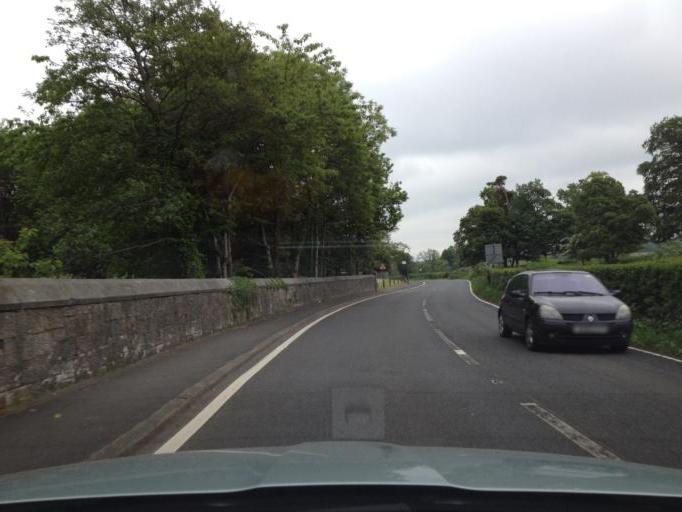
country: GB
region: Scotland
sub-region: Renfrewshire
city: Bishopton
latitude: 55.9161
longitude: -4.4885
